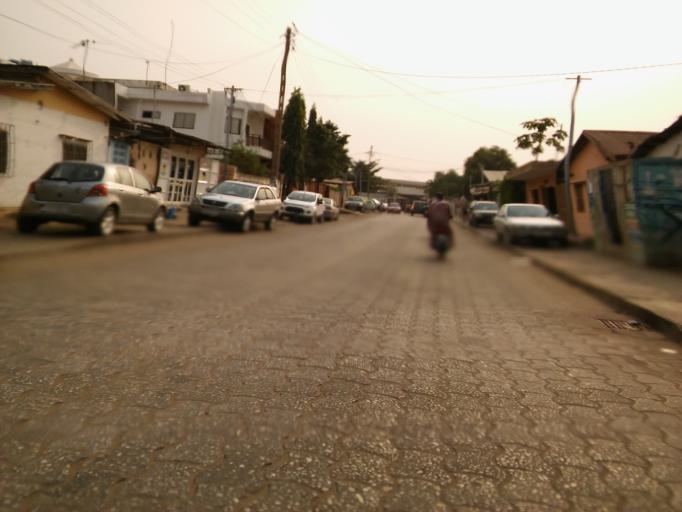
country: BJ
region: Littoral
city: Cotonou
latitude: 6.3605
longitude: 2.4063
